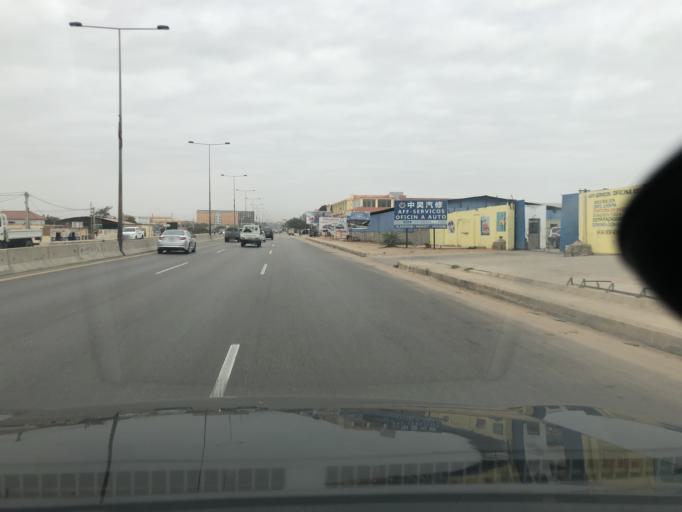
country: AO
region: Luanda
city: Luanda
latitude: -8.9704
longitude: 13.1643
